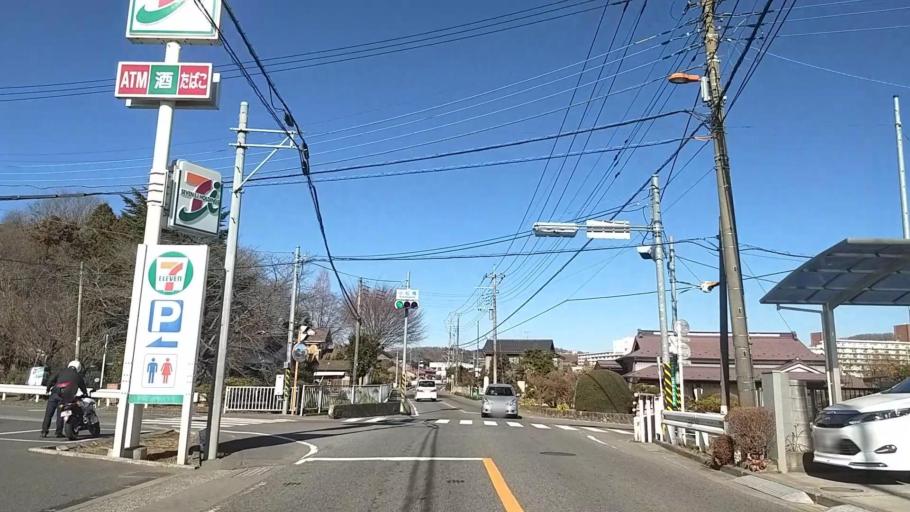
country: JP
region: Tokyo
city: Hachioji
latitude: 35.6037
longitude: 139.2996
